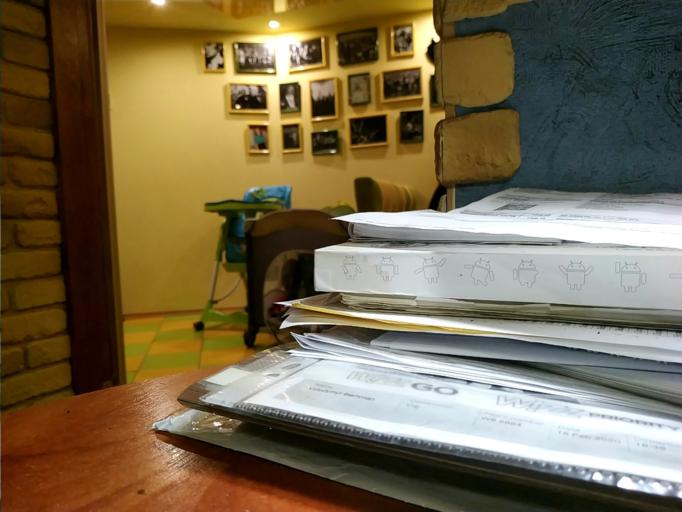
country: RU
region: Arkhangelskaya
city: Kargopol'
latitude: 61.2385
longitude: 39.4772
